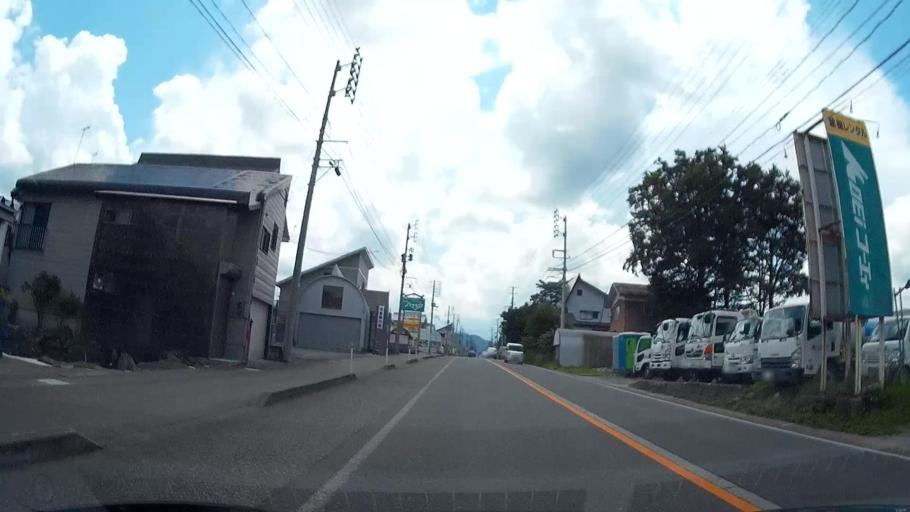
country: JP
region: Niigata
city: Tokamachi
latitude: 37.0254
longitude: 138.6626
